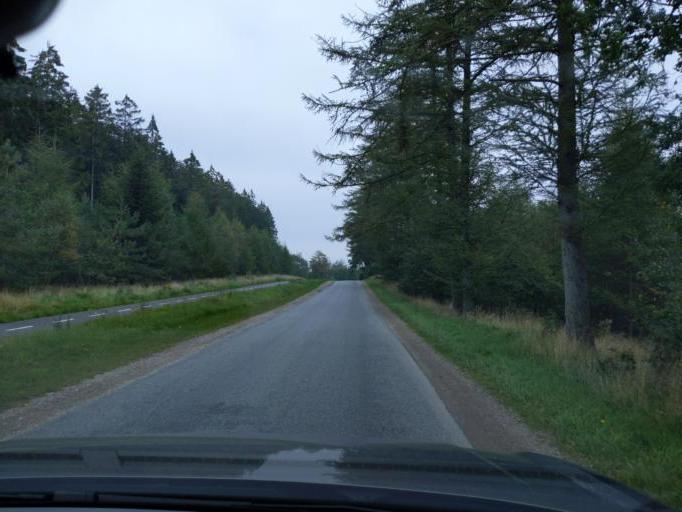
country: DK
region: Central Jutland
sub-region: Viborg Kommune
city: Stoholm
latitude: 56.4524
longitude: 9.2102
